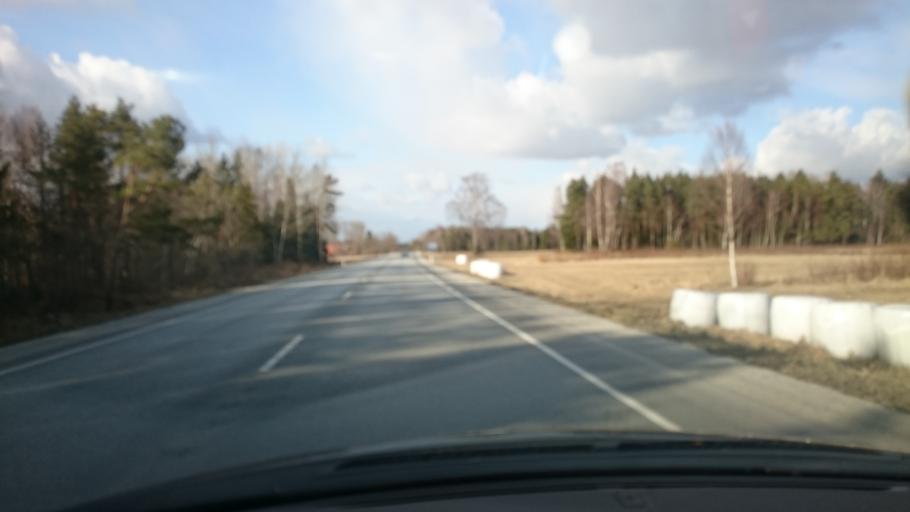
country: EE
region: Harju
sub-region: Nissi vald
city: Riisipere
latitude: 59.1454
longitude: 24.3337
